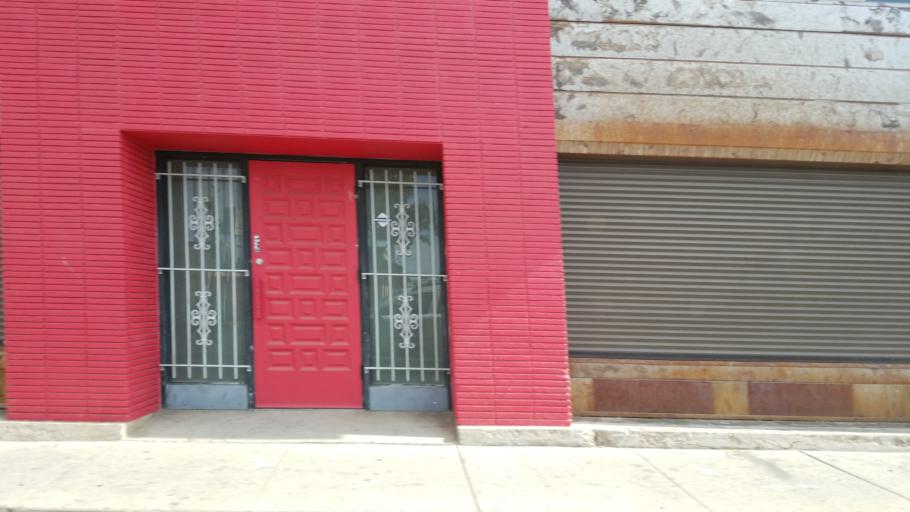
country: US
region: Arizona
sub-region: Maricopa County
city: Phoenix
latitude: 33.4512
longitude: -112.0117
